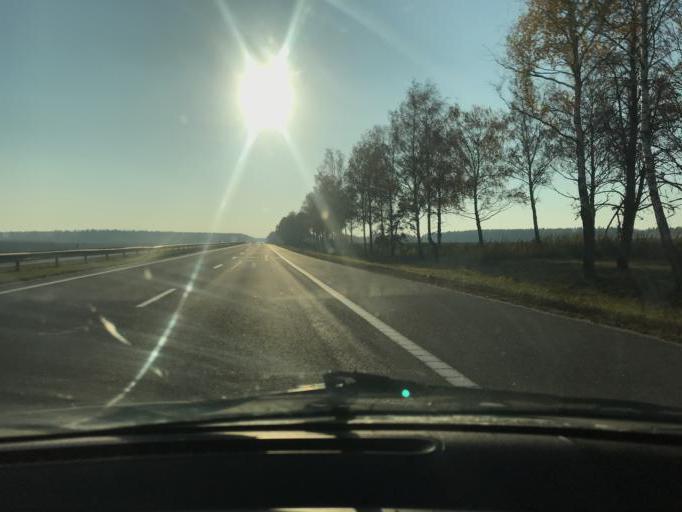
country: BY
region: Minsk
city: Loshnitsa
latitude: 54.2894
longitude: 28.7512
